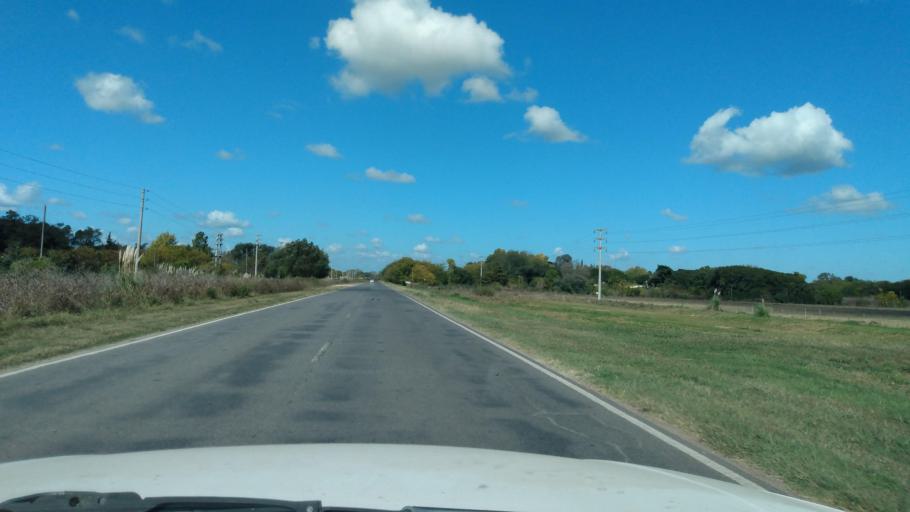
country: AR
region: Buenos Aires
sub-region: Partido de Mercedes
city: Mercedes
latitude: -34.6951
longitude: -59.4039
